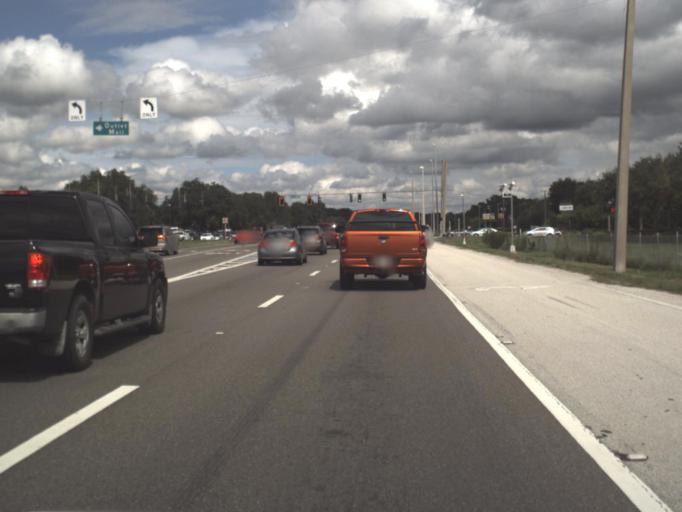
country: US
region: Florida
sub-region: Manatee County
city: Ellenton
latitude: 27.5307
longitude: -82.5041
